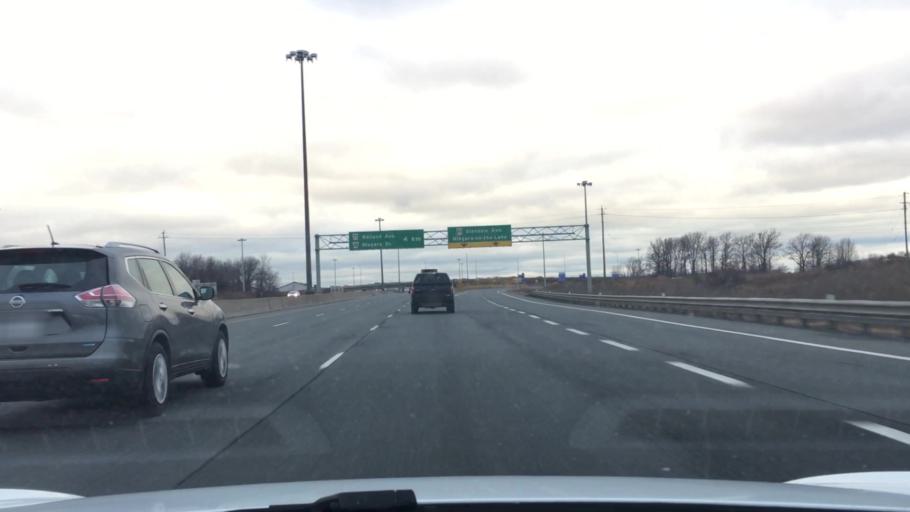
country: CA
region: Ontario
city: Thorold
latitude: 43.1549
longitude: -79.1592
